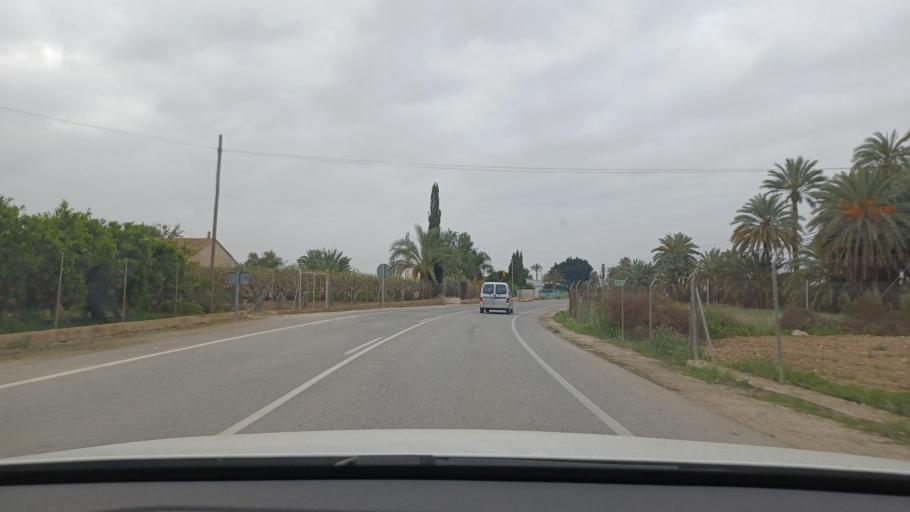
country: ES
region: Valencia
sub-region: Provincia de Alicante
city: Elche
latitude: 38.2272
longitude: -0.7181
